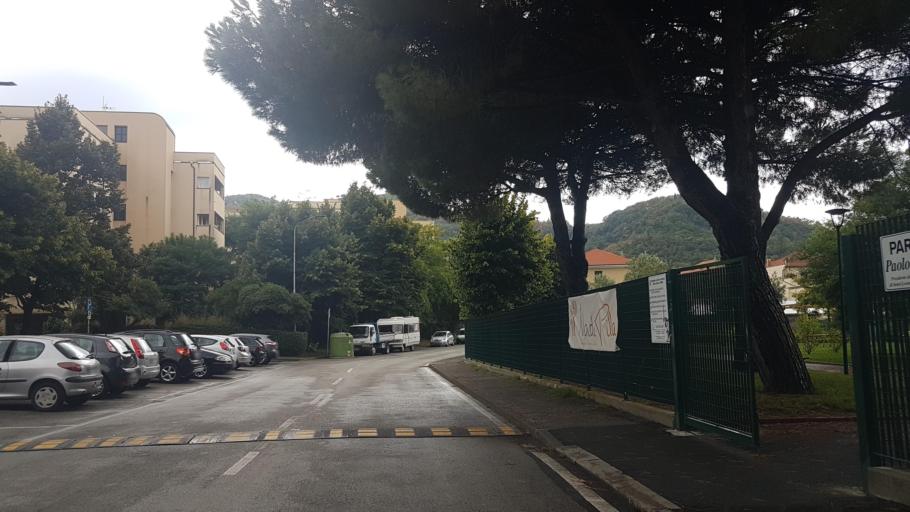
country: IT
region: Liguria
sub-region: Provincia di Genova
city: Sestri Levante
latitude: 44.2717
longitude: 9.4169
